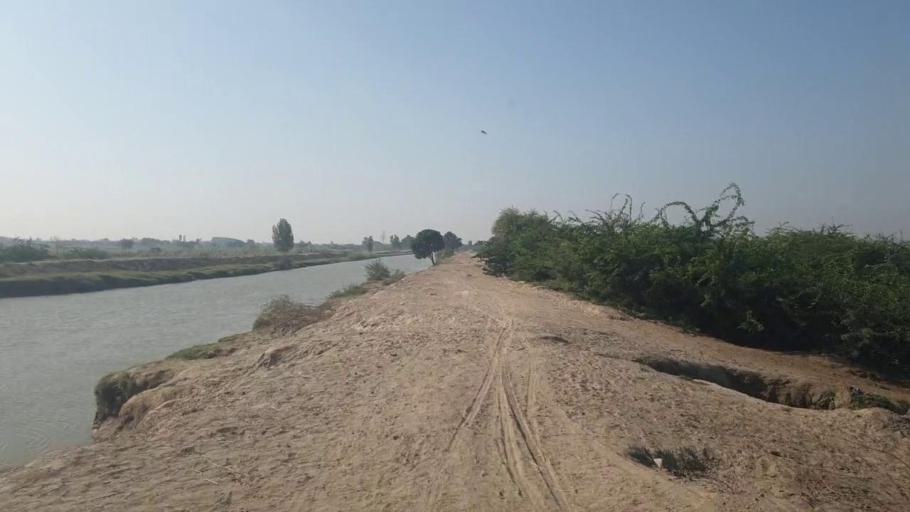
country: PK
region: Sindh
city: Badin
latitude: 24.6923
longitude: 68.8697
